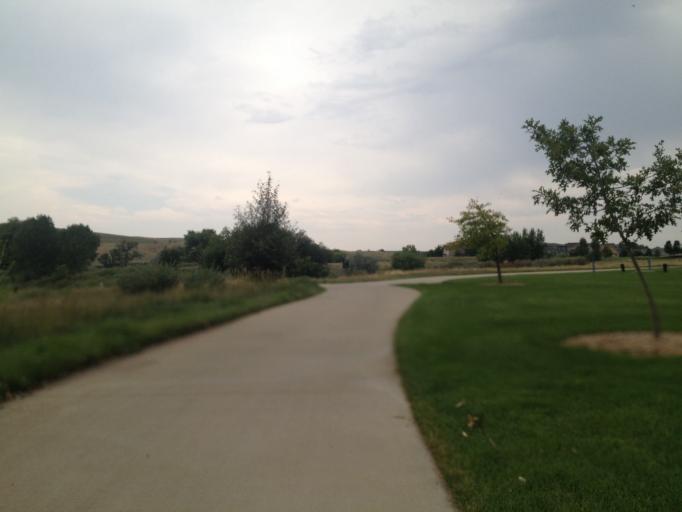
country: US
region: Colorado
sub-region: Boulder County
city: Erie
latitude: 40.0347
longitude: -105.0443
